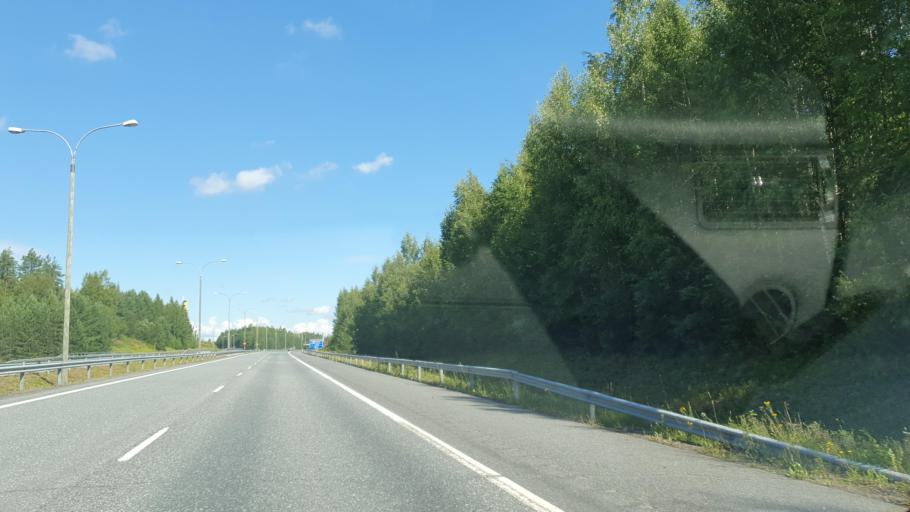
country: FI
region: Northern Savo
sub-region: Ylae-Savo
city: Iisalmi
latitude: 63.5396
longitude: 27.2481
